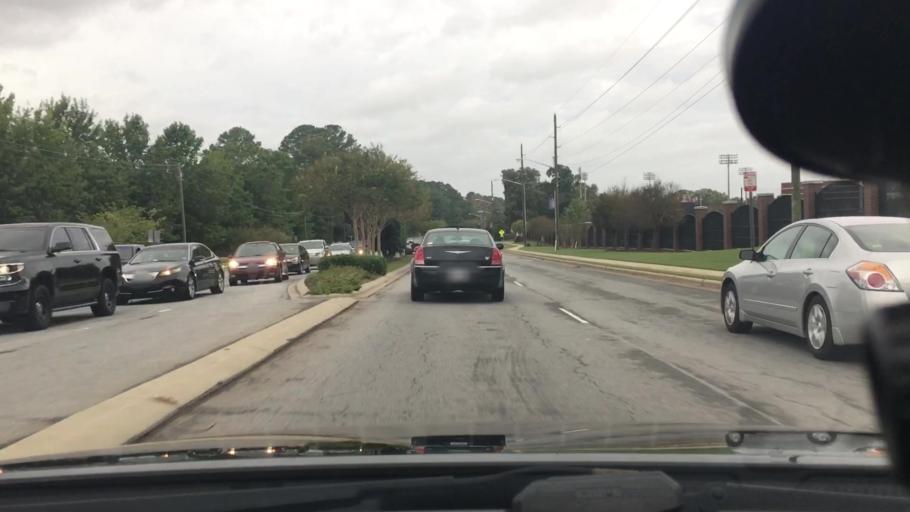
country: US
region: North Carolina
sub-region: Pitt County
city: Greenville
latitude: 35.5903
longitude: -77.3676
